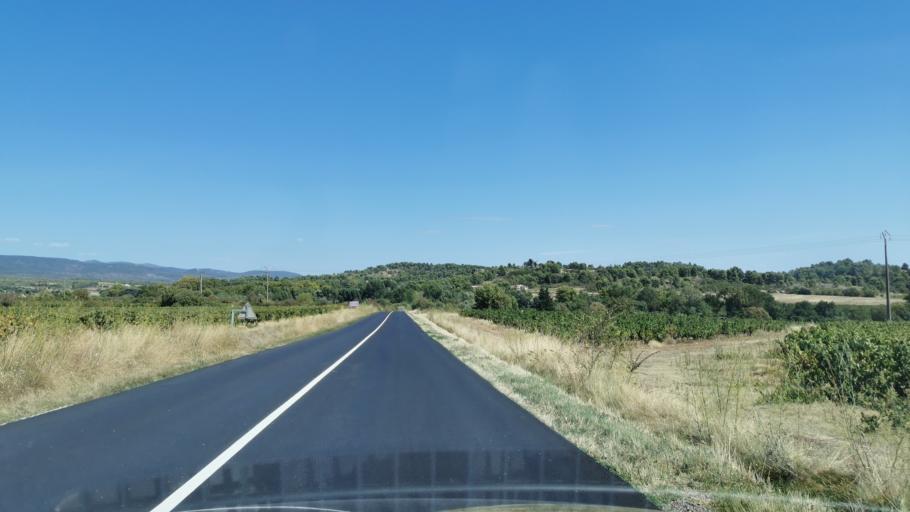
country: FR
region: Languedoc-Roussillon
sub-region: Departement de l'Aude
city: Conques-sur-Orbiel
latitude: 43.2781
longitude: 2.4304
